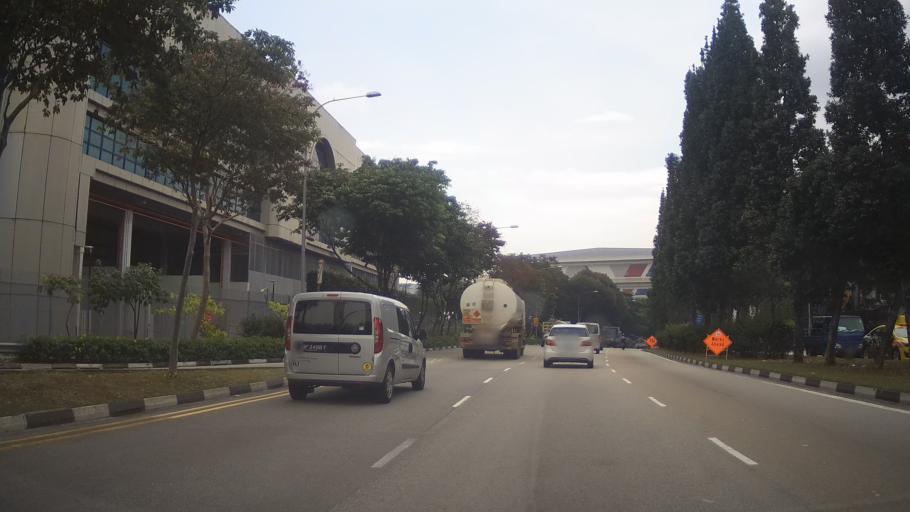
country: SG
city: Singapore
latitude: 1.3211
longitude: 103.7103
